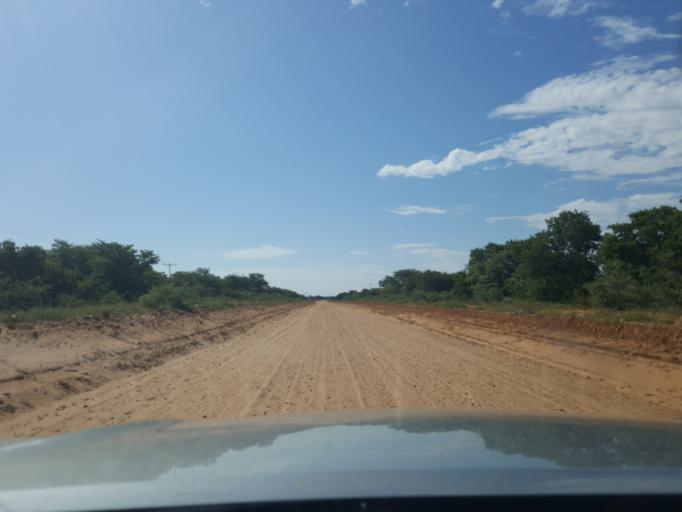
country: BW
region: Kweneng
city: Khudumelapye
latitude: -23.7060
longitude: 24.7252
